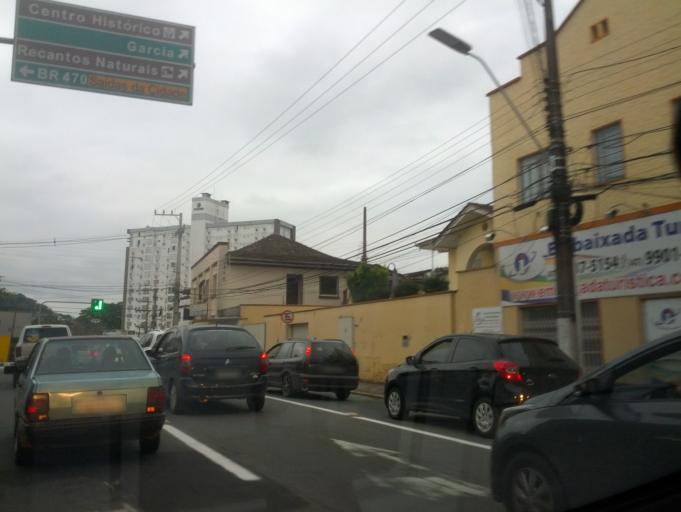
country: BR
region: Santa Catarina
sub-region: Blumenau
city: Blumenau
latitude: -26.9145
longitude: -49.0758
